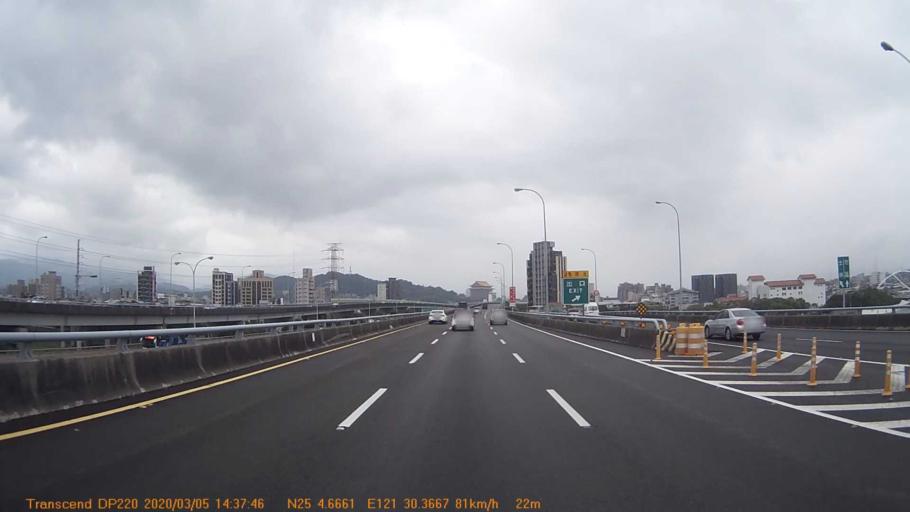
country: TW
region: Taipei
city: Taipei
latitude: 25.0775
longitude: 121.5060
